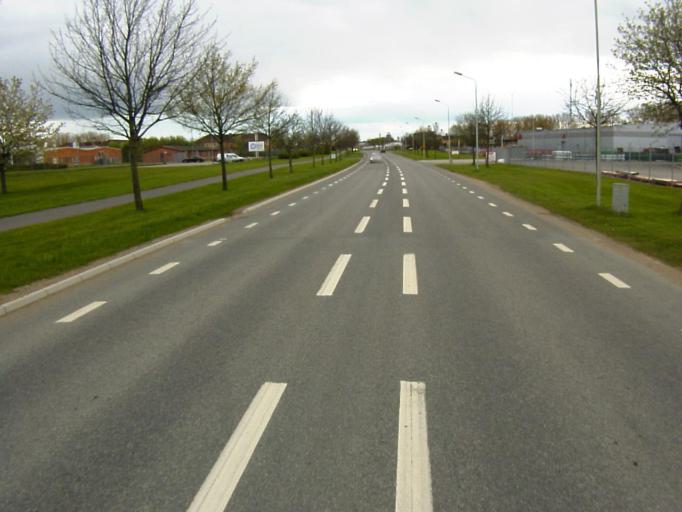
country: SE
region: Skane
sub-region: Kristianstads Kommun
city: Kristianstad
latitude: 56.0548
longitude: 14.1670
